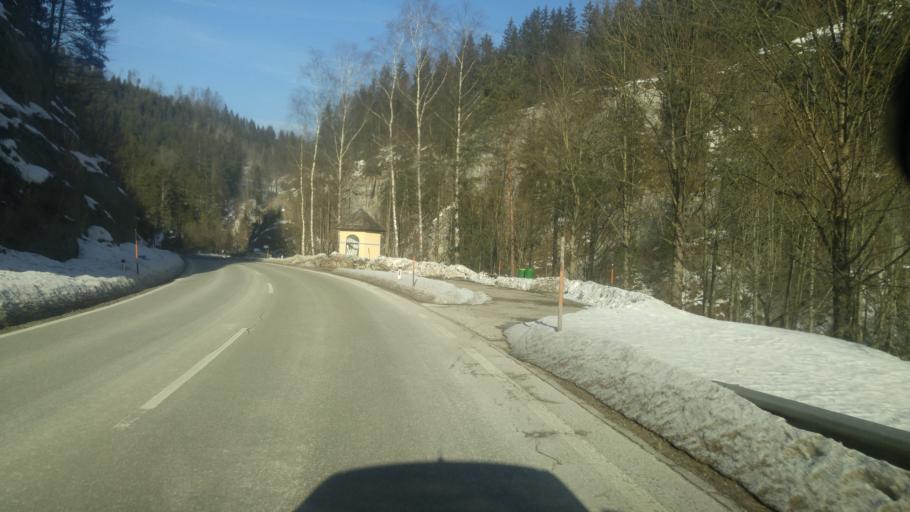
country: AT
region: Lower Austria
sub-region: Politischer Bezirk Lilienfeld
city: Turnitz
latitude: 47.9451
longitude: 15.5182
